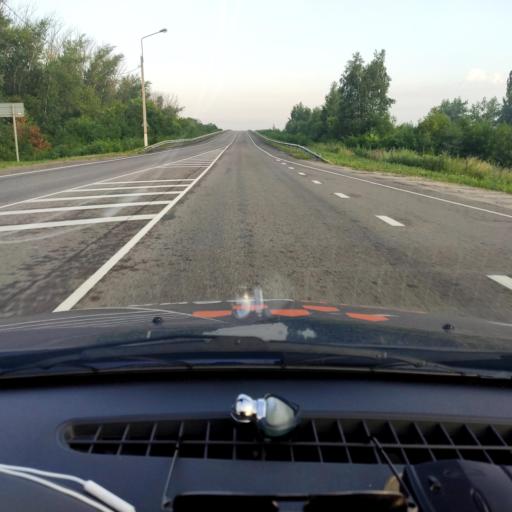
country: RU
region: Lipetsk
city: Yelets
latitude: 52.5610
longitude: 38.6861
